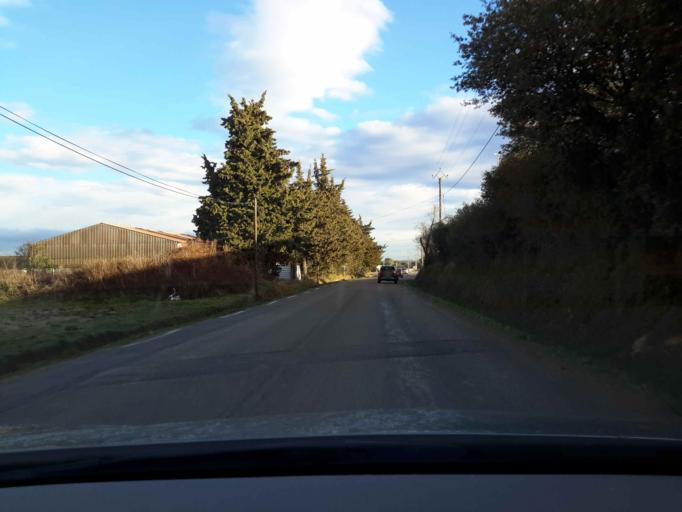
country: FR
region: Languedoc-Roussillon
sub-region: Departement du Gard
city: Generac
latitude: 43.7507
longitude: 4.3424
